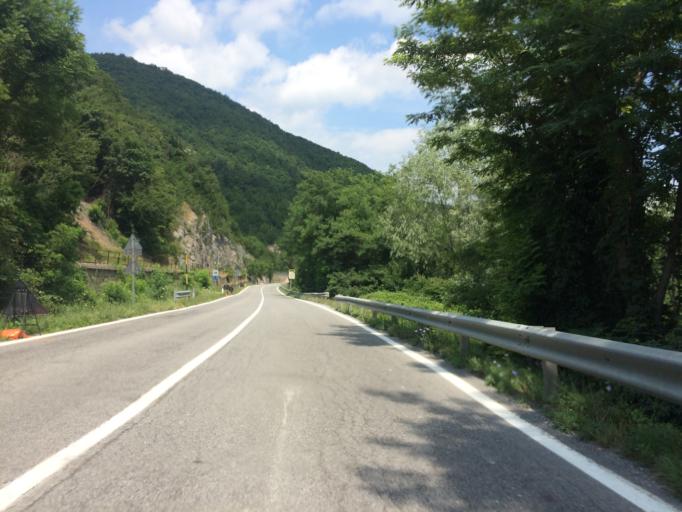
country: IT
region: Piedmont
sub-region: Provincia di Cuneo
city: Bagnasco
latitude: 44.2811
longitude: 8.0345
